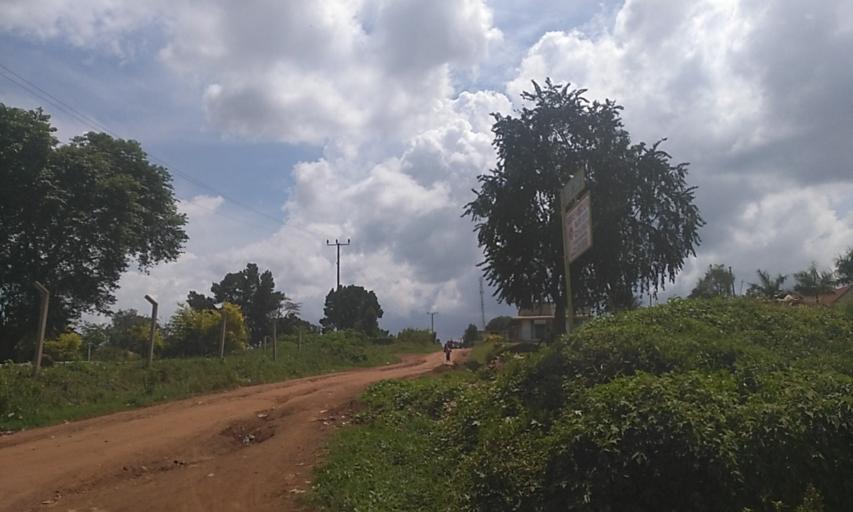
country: UG
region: Central Region
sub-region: Wakiso District
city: Wakiso
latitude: 0.3969
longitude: 32.4757
